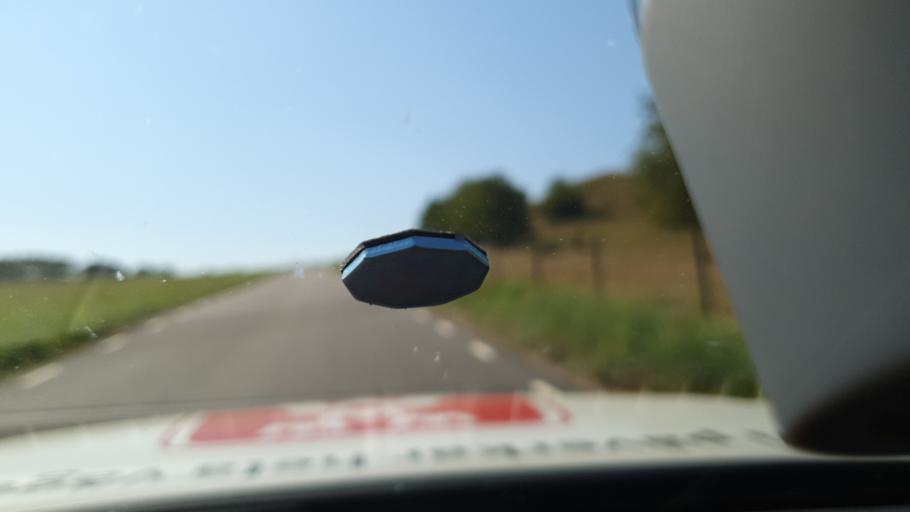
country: SE
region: Skane
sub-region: Sjobo Kommun
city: Blentarp
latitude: 55.5625
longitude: 13.5713
